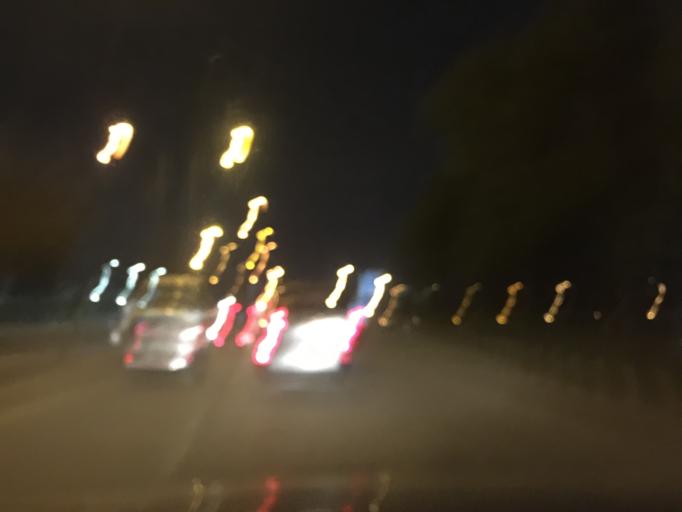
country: JO
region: Amman
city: Umm as Summaq
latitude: 31.9083
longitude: 35.8549
